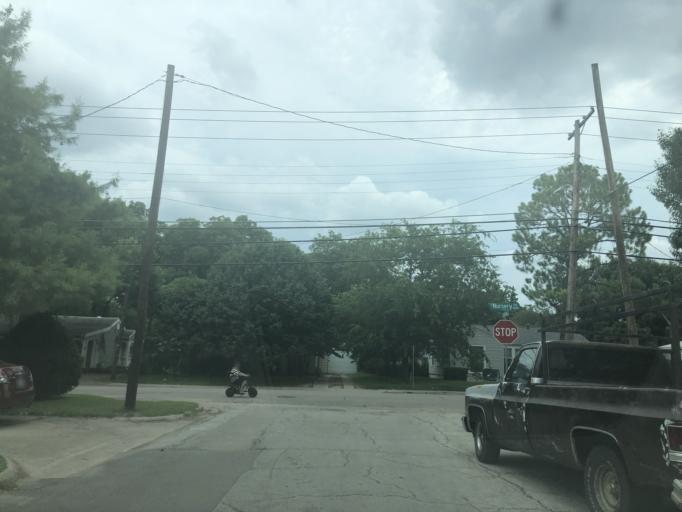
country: US
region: Texas
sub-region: Dallas County
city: Irving
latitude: 32.8026
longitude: -96.9343
